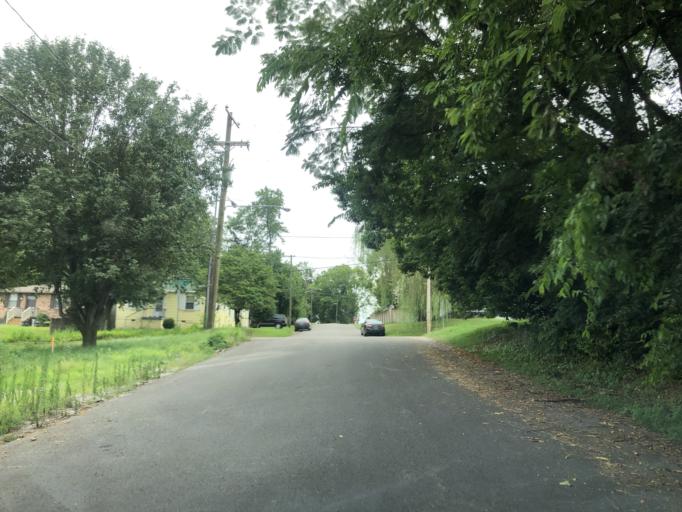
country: US
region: Tennessee
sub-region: Davidson County
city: Nashville
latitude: 36.1682
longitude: -86.7361
